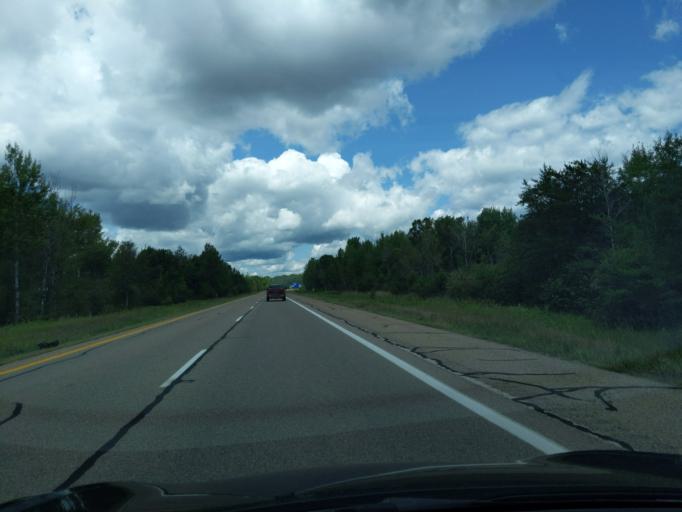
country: US
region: Michigan
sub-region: Roscommon County
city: Houghton Lake
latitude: 44.3054
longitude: -84.8031
